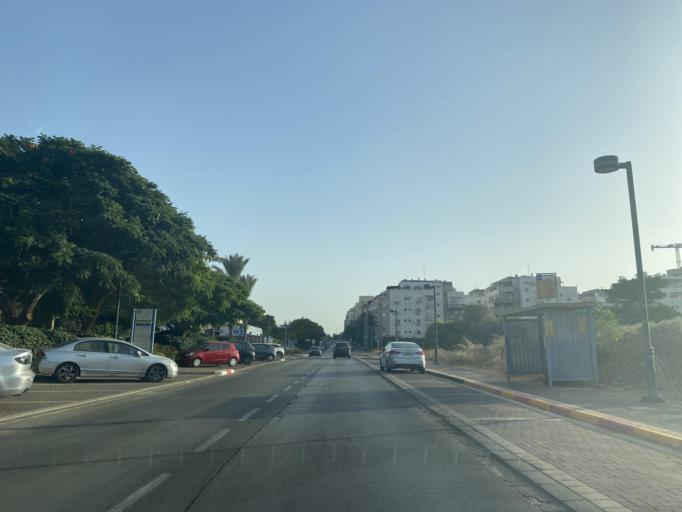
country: IL
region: Central District
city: Kfar Saba
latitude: 32.1633
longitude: 34.9075
